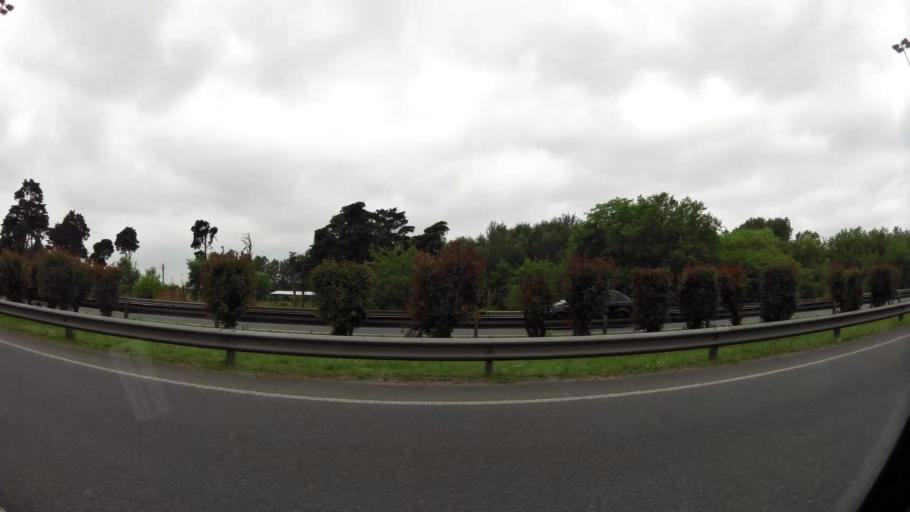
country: AR
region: Buenos Aires
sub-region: Partido de Ezeiza
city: Ezeiza
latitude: -34.8028
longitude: -58.5132
